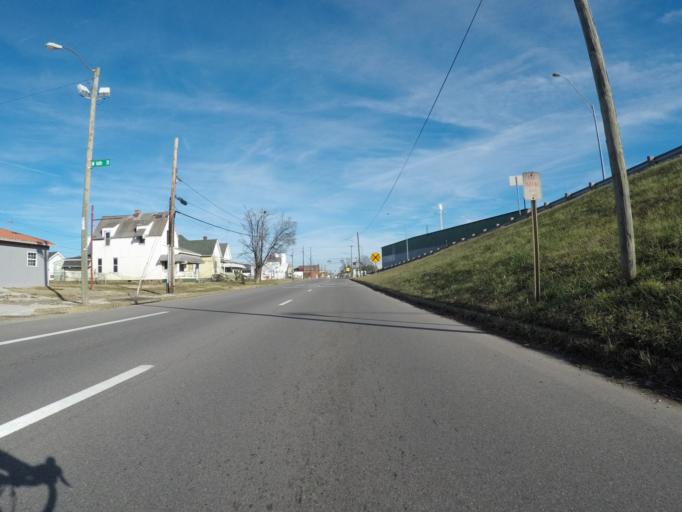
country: US
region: West Virginia
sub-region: Cabell County
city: Huntington
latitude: 38.4111
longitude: -82.4829
